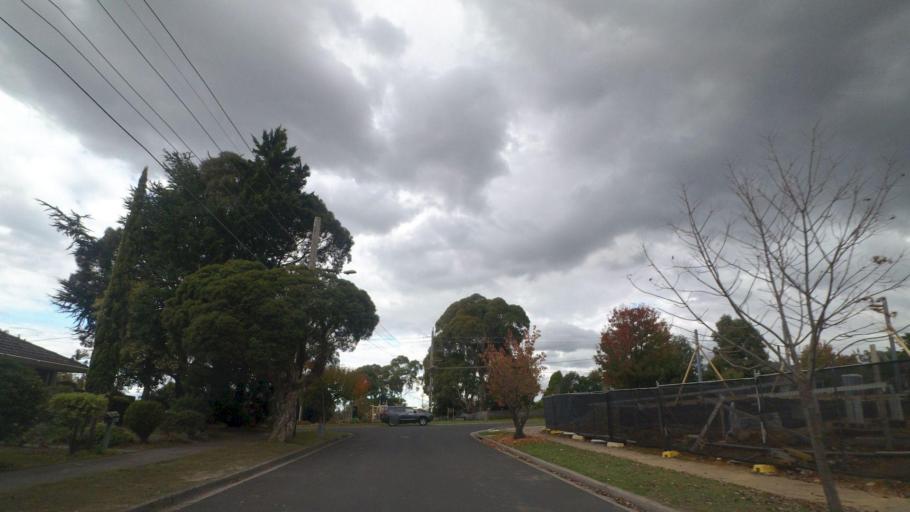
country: AU
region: Victoria
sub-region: Manningham
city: Doncaster East
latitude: -37.7850
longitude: 145.1484
